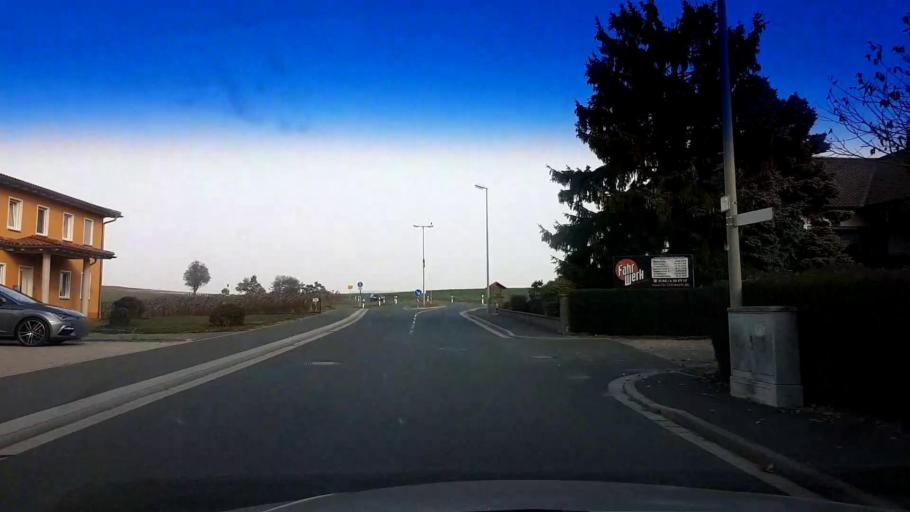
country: DE
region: Bavaria
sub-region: Upper Franconia
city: Altenkunstadt
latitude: 50.1112
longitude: 11.2540
